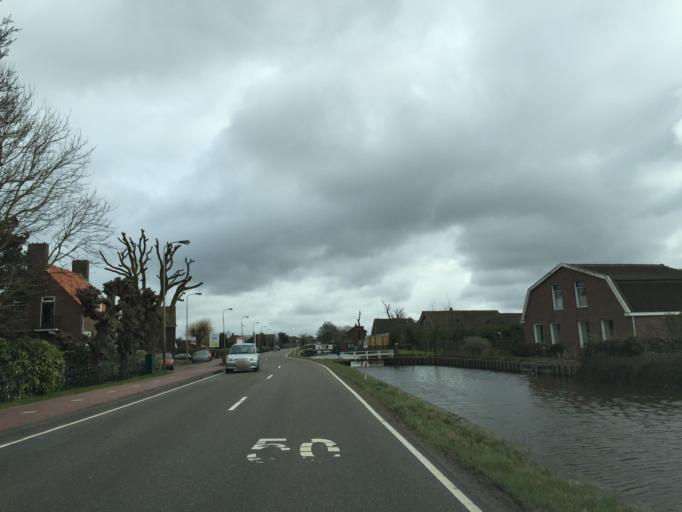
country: NL
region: South Holland
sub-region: Gemeente Lansingerland
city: Berkel en Rodenrijs
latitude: 52.0234
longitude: 4.4824
